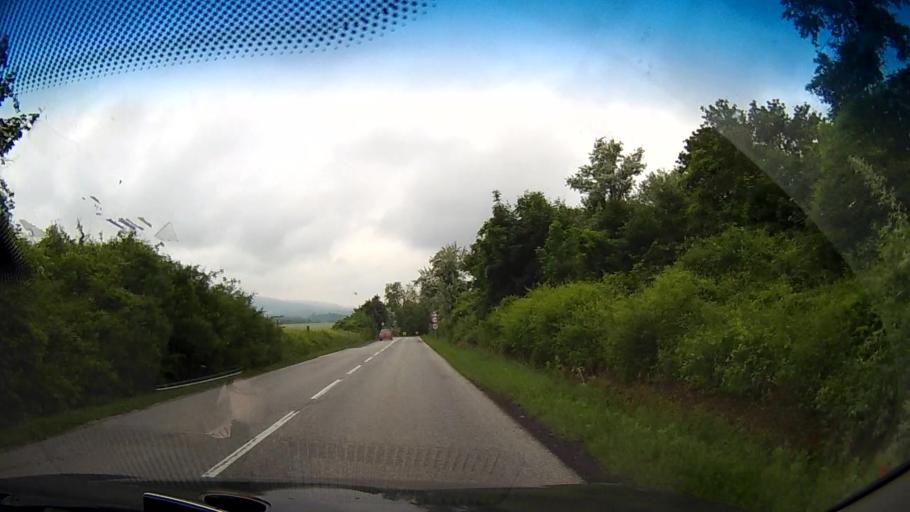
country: HU
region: Pest
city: Perbal
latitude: 47.6092
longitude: 18.7708
